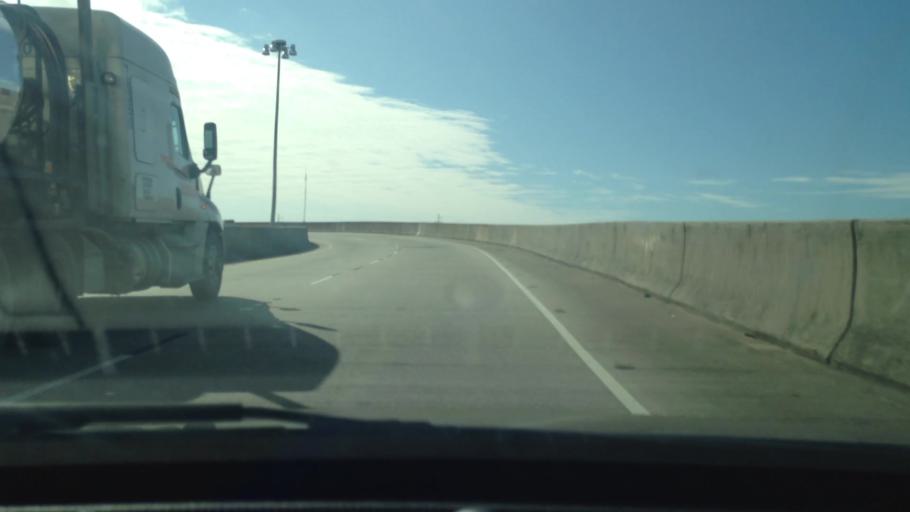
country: US
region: Louisiana
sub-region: Jefferson Parish
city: Terrytown
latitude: 29.9314
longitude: -90.0388
